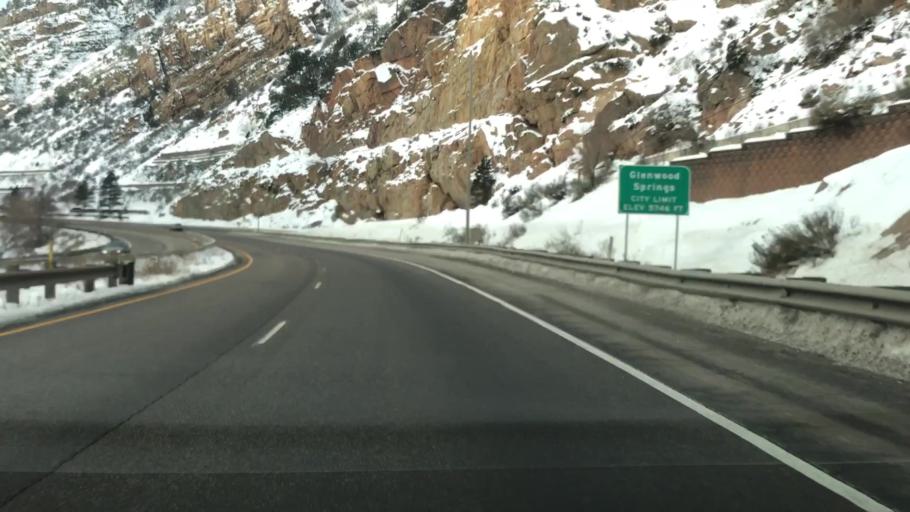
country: US
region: Colorado
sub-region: Garfield County
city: Glenwood Springs
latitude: 39.5615
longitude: -107.3088
